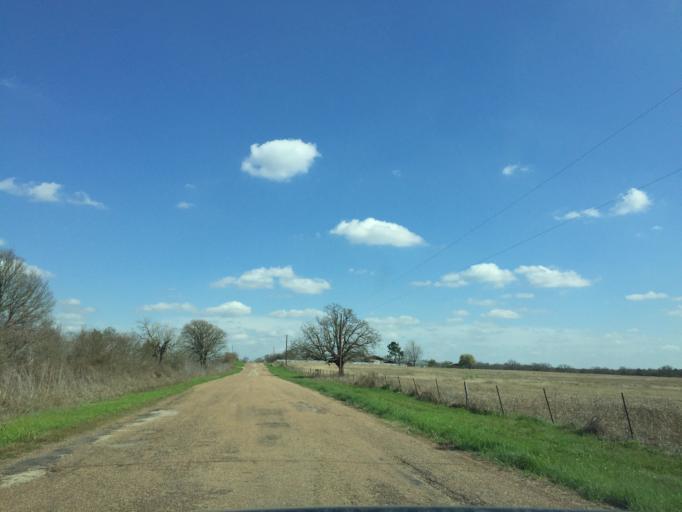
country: US
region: Texas
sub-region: Milam County
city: Thorndale
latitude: 30.5572
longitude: -97.1671
